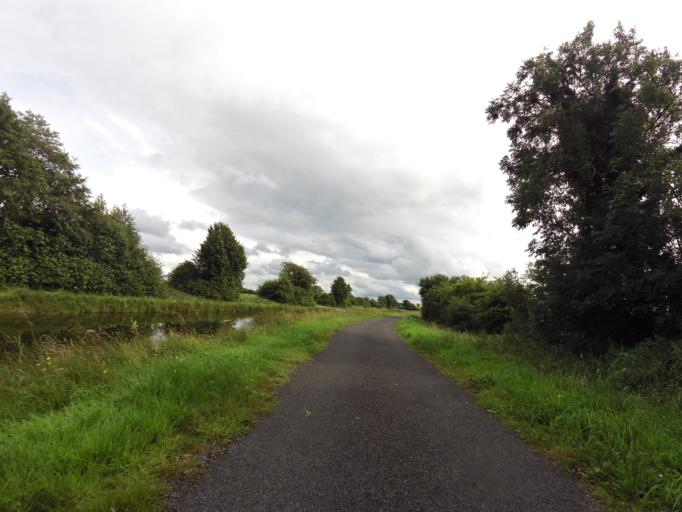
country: IE
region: Leinster
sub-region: An Iarmhi
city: An Muileann gCearr
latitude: 53.5615
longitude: -7.5037
